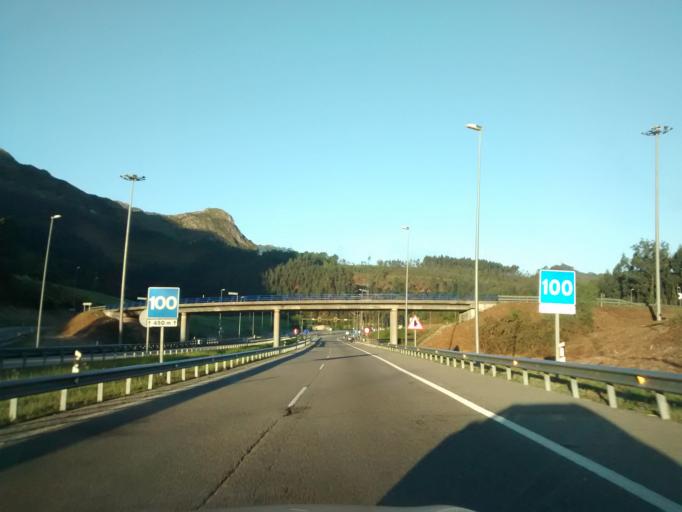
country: ES
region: Asturias
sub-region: Province of Asturias
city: Ribadesella
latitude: 43.4386
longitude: -5.0412
